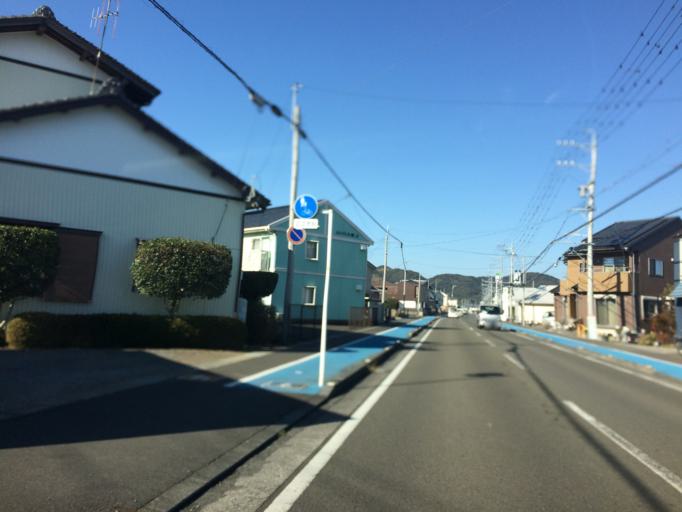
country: JP
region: Shizuoka
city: Shimada
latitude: 34.8346
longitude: 138.2166
